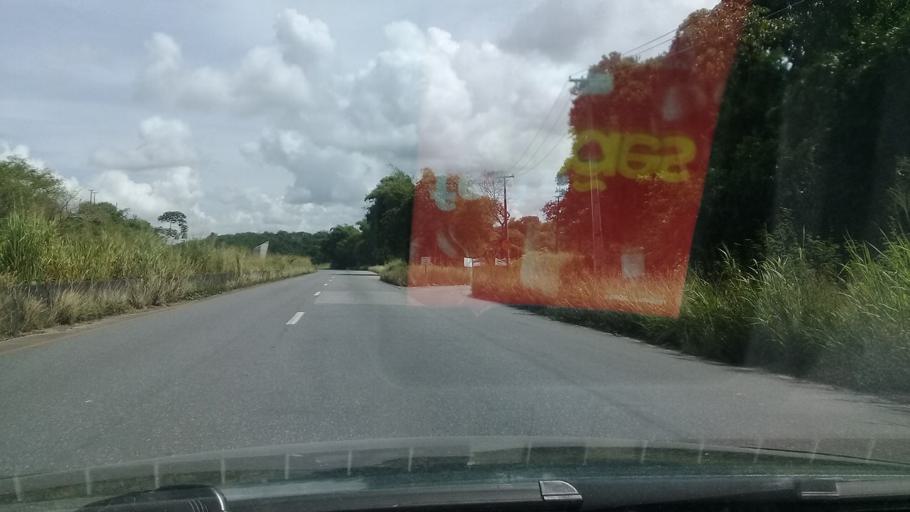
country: BR
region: Pernambuco
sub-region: Moreno
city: Moreno
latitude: -8.0955
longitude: -35.0771
